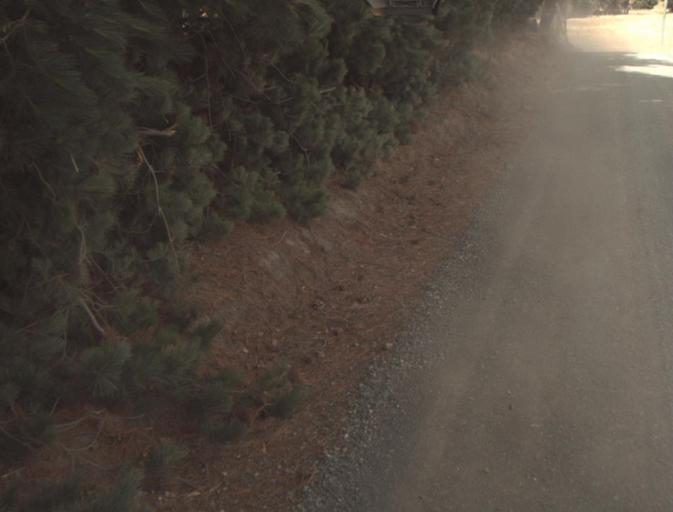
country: AU
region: Tasmania
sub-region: Launceston
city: Mayfield
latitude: -41.1736
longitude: 147.2123
